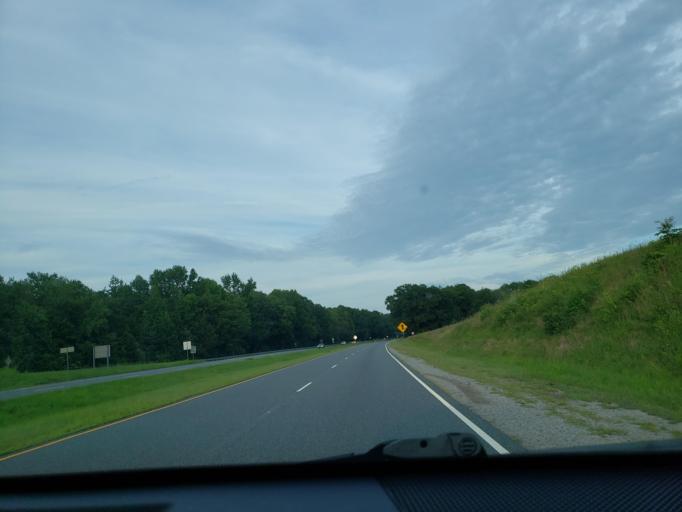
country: US
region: Virginia
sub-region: Brunswick County
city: Lawrenceville
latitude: 36.7483
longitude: -77.8545
